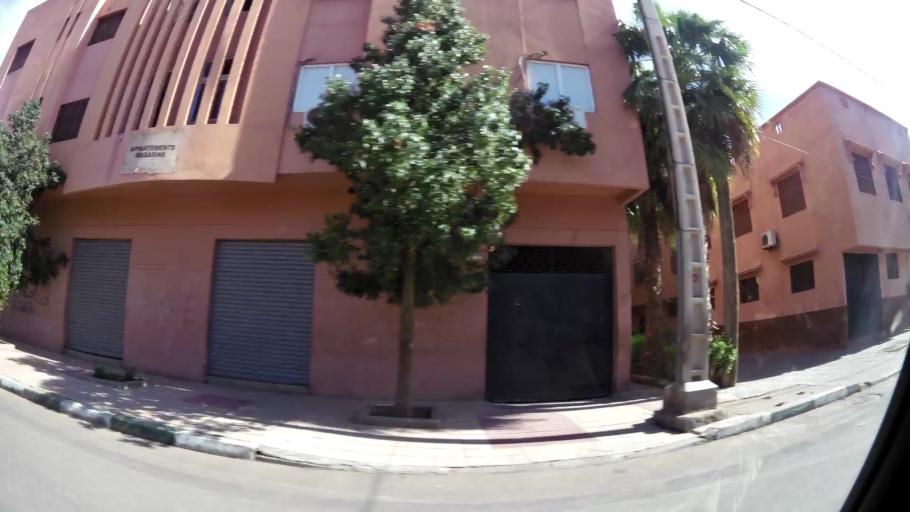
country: MA
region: Marrakech-Tensift-Al Haouz
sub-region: Marrakech
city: Marrakesh
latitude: 31.6436
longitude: -7.9782
